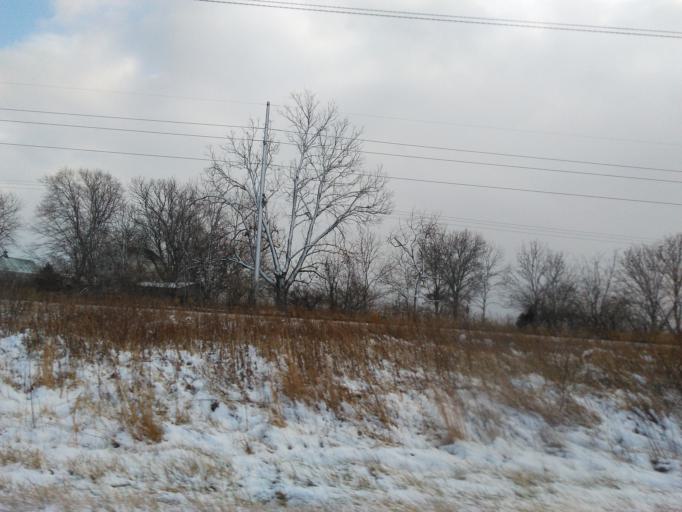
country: US
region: Illinois
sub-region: Madison County
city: Highland
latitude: 38.7327
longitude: -89.7195
